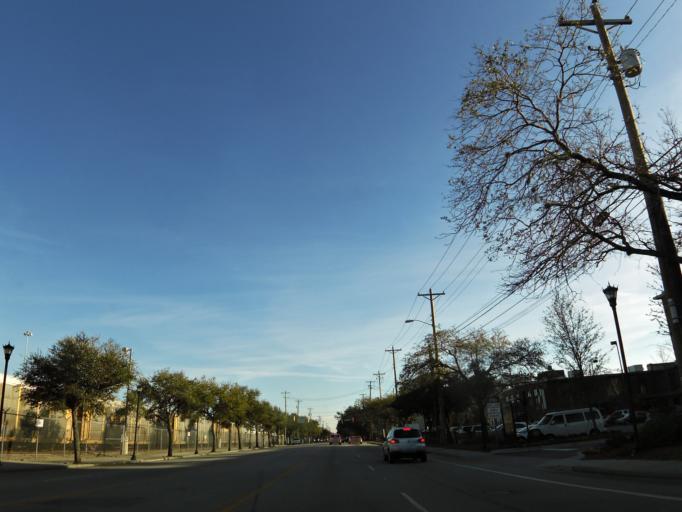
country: US
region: South Carolina
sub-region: Charleston County
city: Charleston
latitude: 32.7982
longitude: -79.9343
